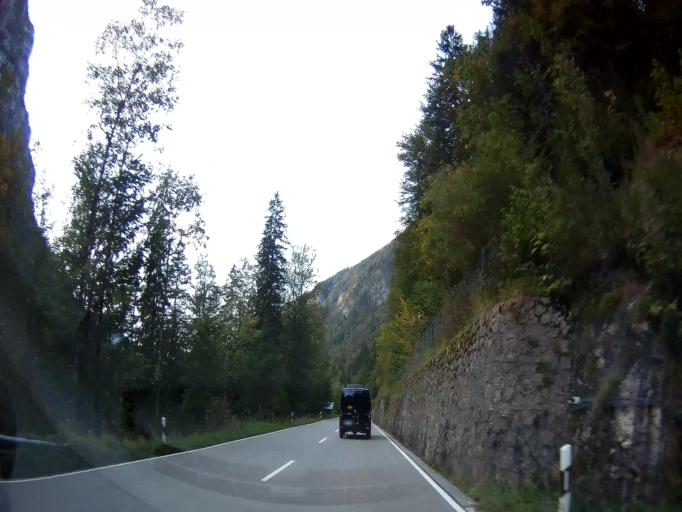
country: DE
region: Bavaria
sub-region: Upper Bavaria
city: Schneizlreuth
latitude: 47.6541
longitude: 12.8499
